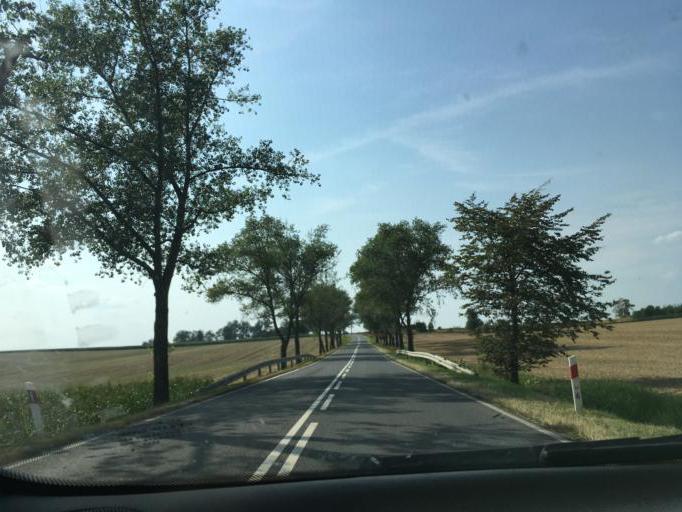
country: PL
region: Opole Voivodeship
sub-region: Powiat prudnicki
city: Moszczanka
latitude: 50.4214
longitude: 17.4628
